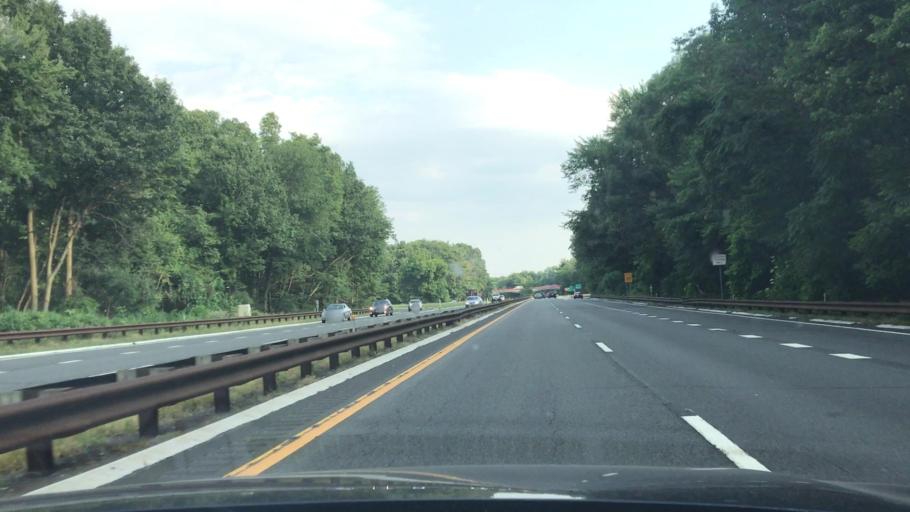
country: US
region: New York
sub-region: Rockland County
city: Bardonia
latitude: 41.0951
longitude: -73.9911
